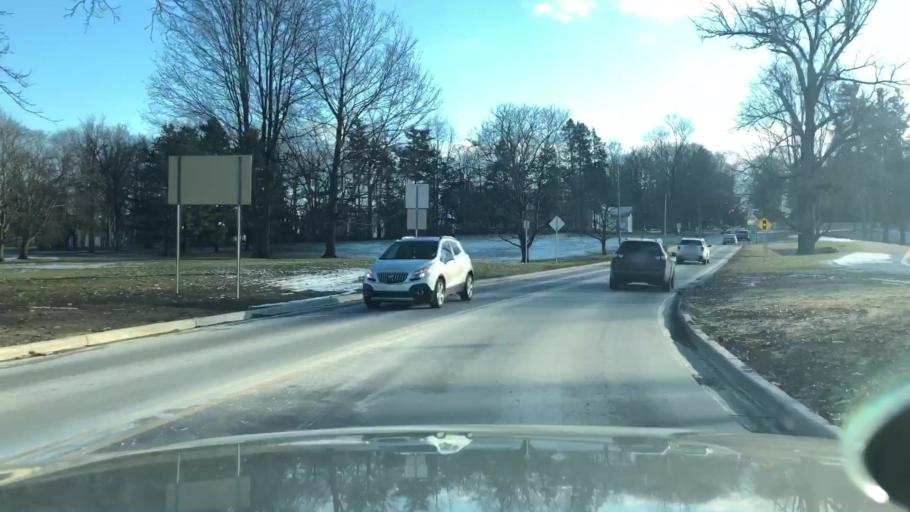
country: US
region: Michigan
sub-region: Jackson County
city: Jackson
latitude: 42.2168
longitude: -84.4183
